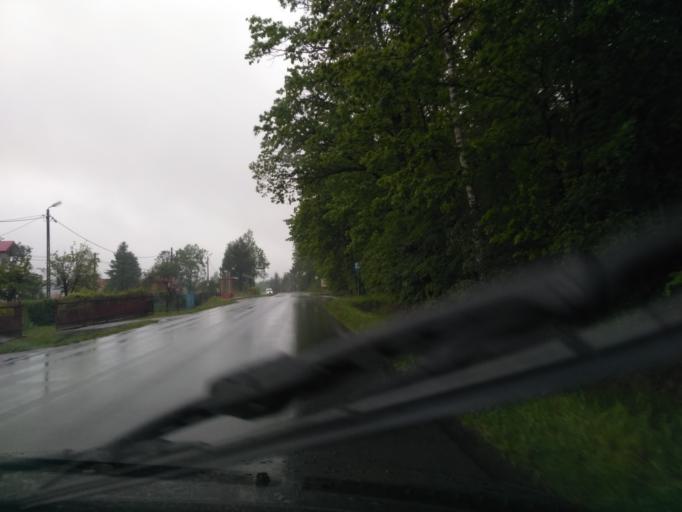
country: PL
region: Subcarpathian Voivodeship
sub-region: Powiat jasielski
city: Debowiec
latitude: 49.6538
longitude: 21.4140
